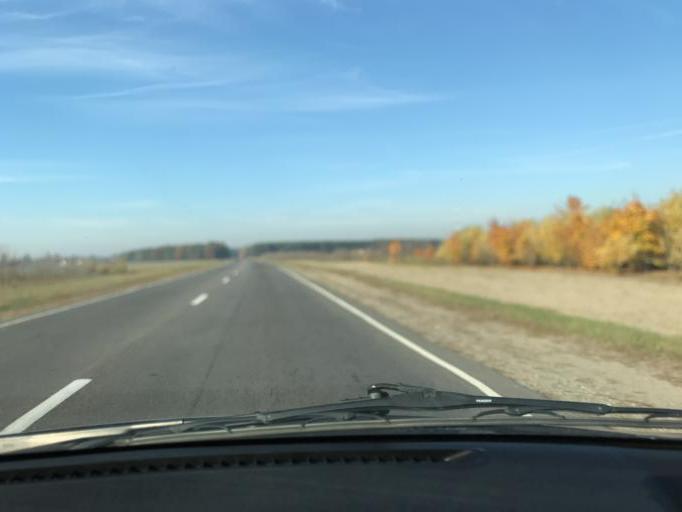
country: BY
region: Brest
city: Luninyets
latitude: 52.2752
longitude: 26.9740
